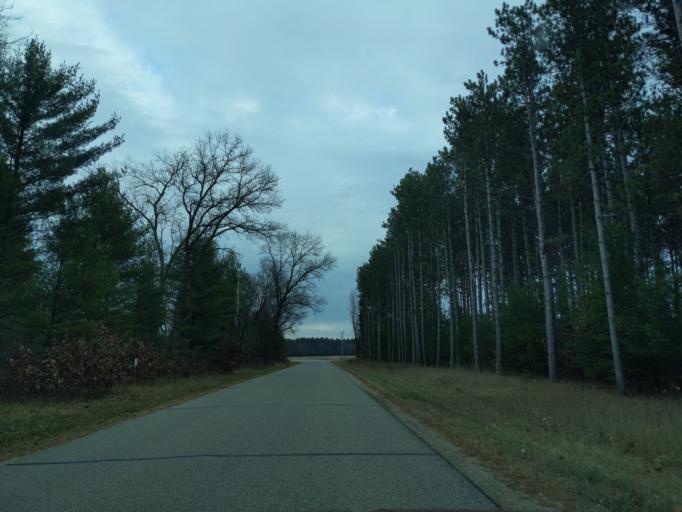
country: US
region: Wisconsin
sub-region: Waushara County
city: Wautoma
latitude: 44.0449
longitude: -89.2888
